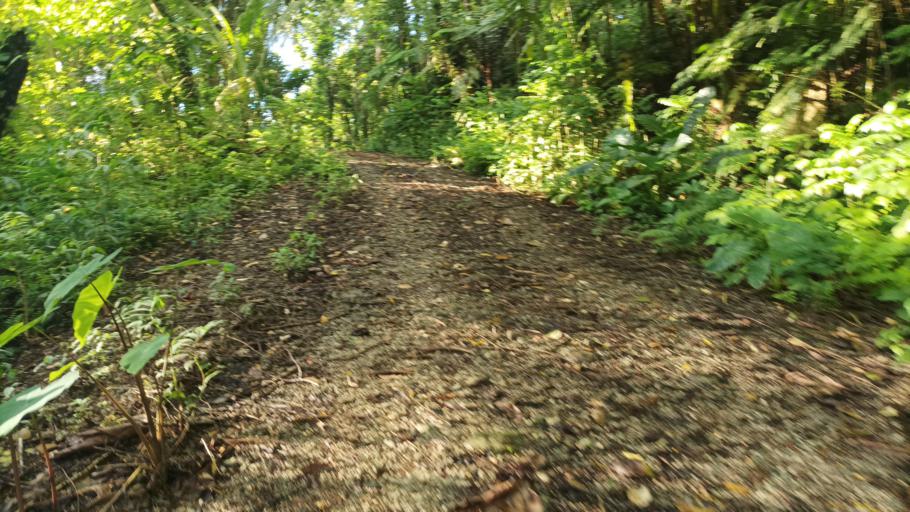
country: FM
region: Pohnpei
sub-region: Kolonia Municipality
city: Kolonia Town
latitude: 6.9664
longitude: 158.1864
